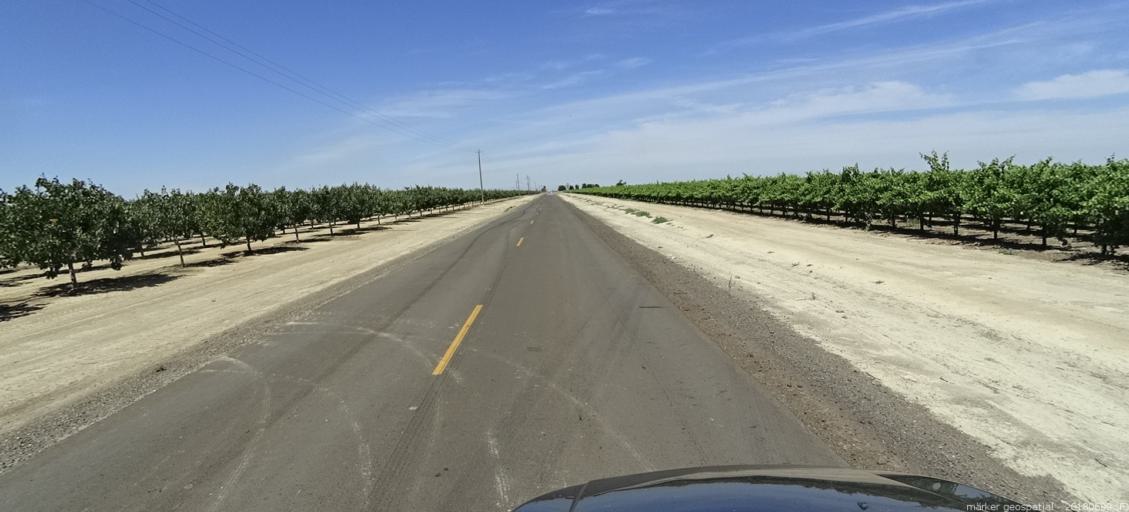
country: US
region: California
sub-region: Fresno County
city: Firebaugh
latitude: 36.9525
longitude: -120.3922
